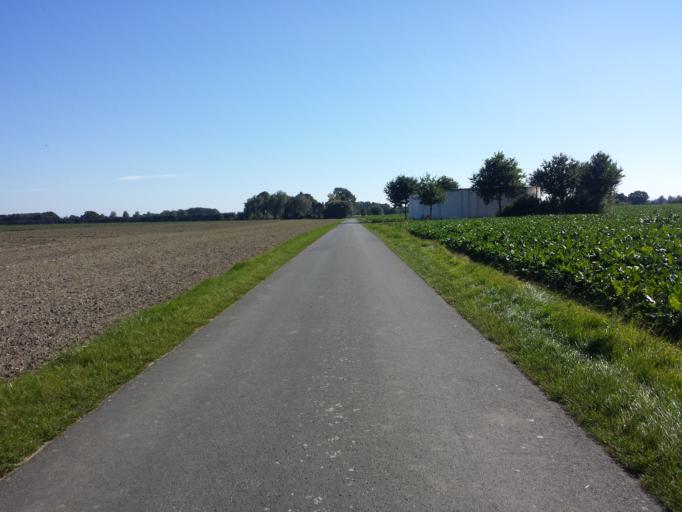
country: DE
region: North Rhine-Westphalia
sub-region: Regierungsbezirk Detmold
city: Langenberg
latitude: 51.7461
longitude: 8.3345
